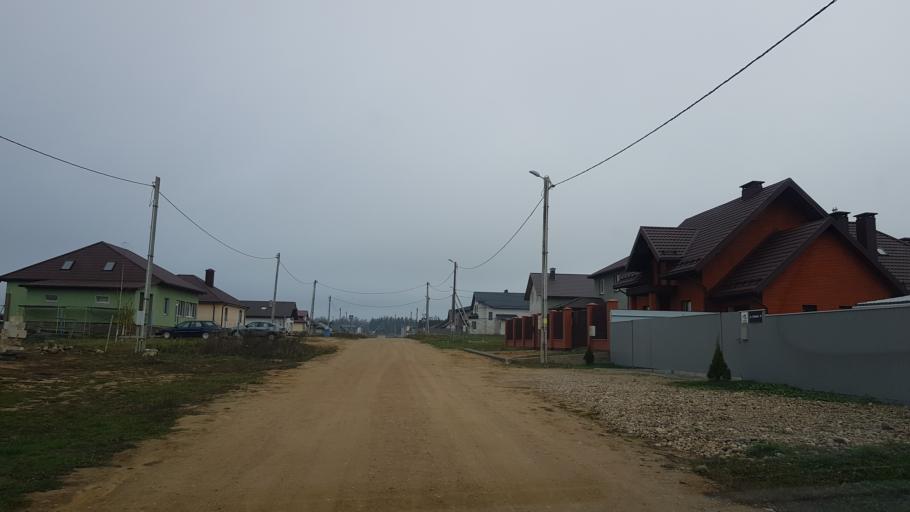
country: BY
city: Fanipol
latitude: 53.7265
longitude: 27.3246
